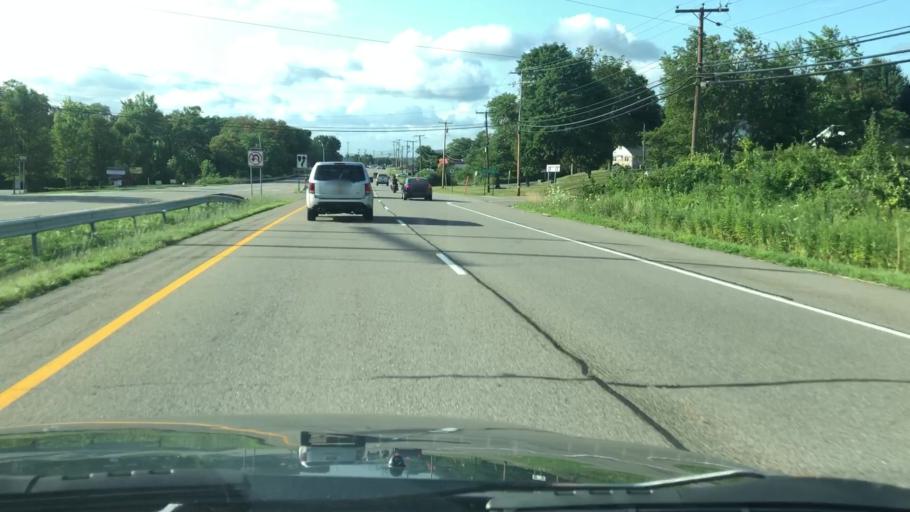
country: US
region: New York
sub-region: Dutchess County
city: Wappingers Falls
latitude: 41.5692
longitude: -73.9084
